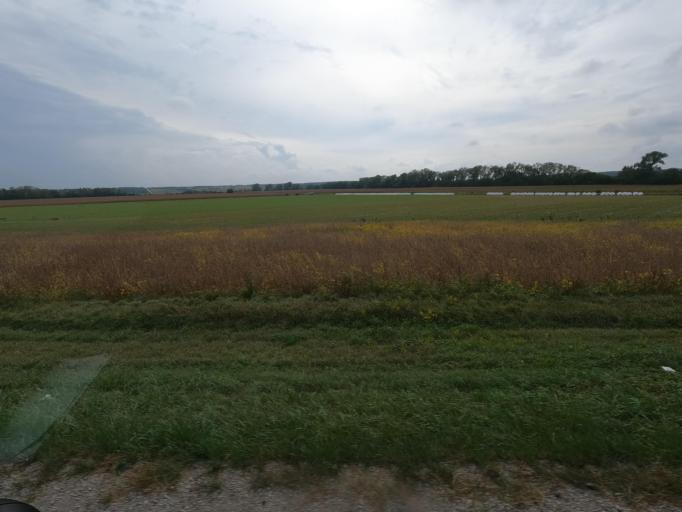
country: US
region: Iowa
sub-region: Jefferson County
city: Fairfield
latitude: 40.8866
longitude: -92.1667
